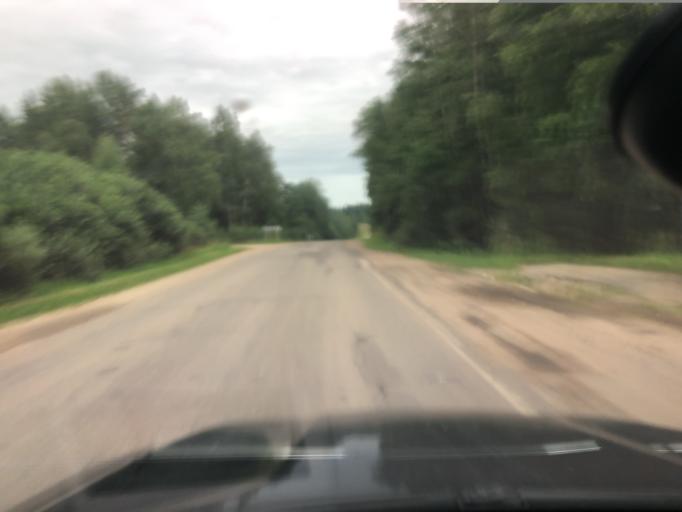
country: RU
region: Jaroslavl
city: Petrovsk
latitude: 56.9865
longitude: 39.1549
